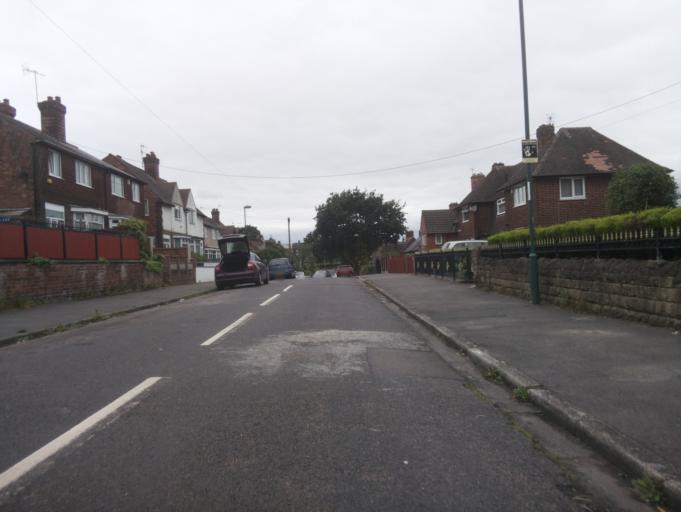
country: GB
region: England
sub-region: Nottinghamshire
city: Arnold
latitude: 52.9867
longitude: -1.1484
